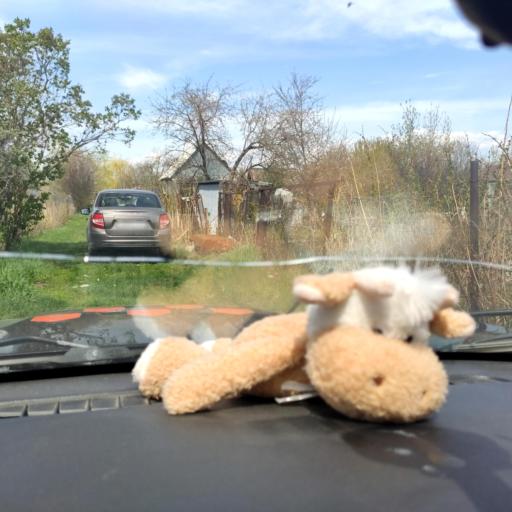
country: RU
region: Samara
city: Podstepki
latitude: 53.5118
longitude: 49.0855
